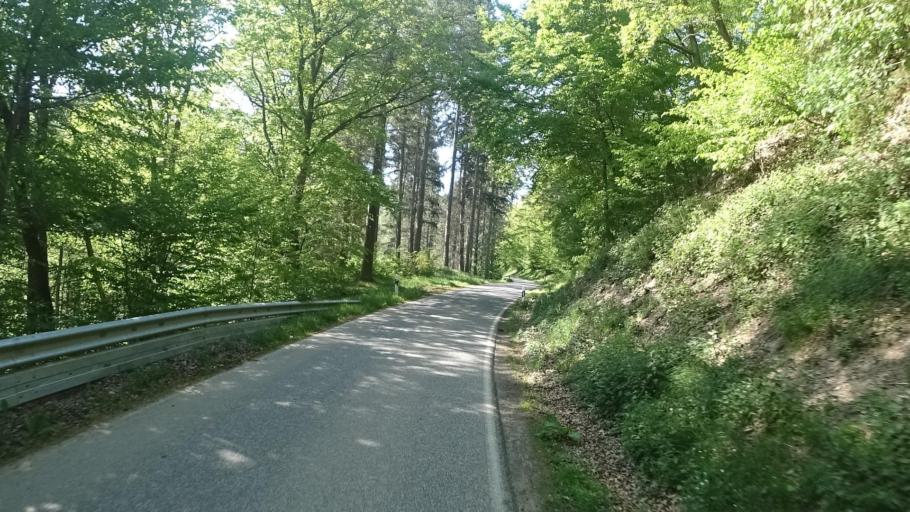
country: DE
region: Rheinland-Pfalz
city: Sierscheid
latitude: 50.4746
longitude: 6.9187
